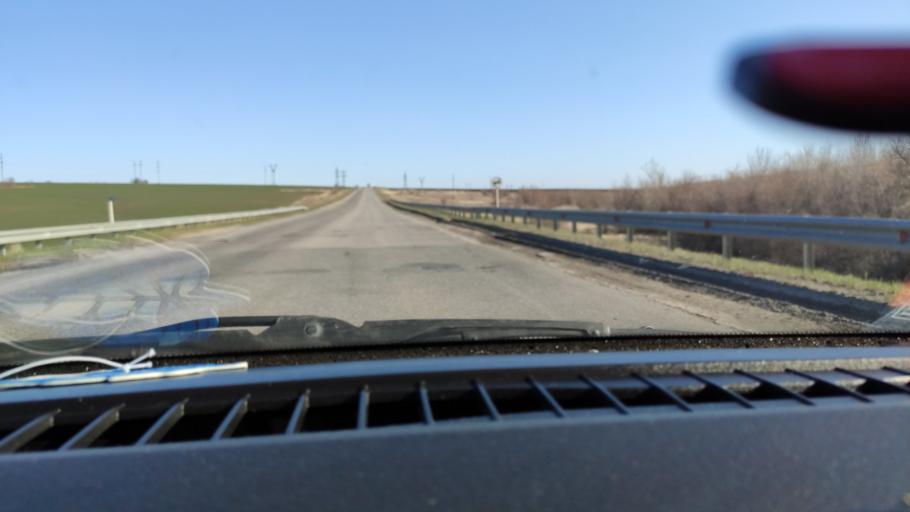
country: RU
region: Samara
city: Varlamovo
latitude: 53.0730
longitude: 48.3541
